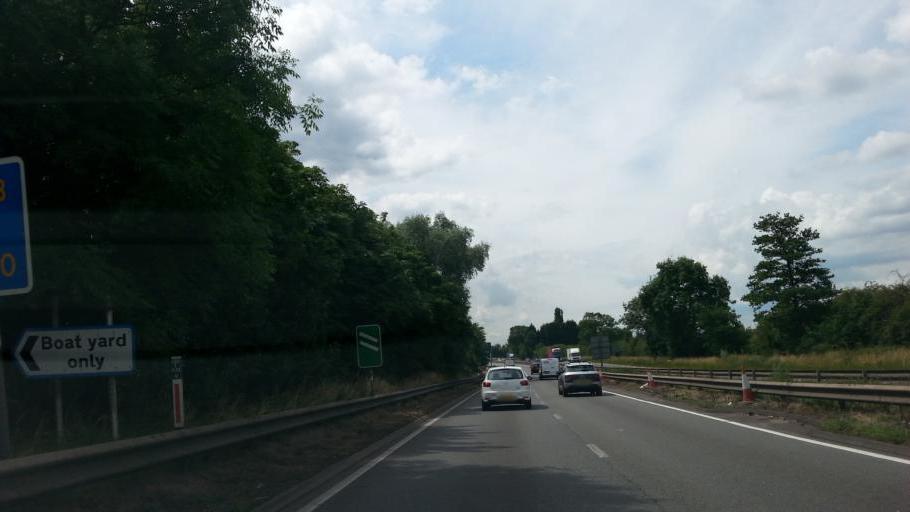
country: GB
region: England
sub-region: Staffordshire
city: Whittington
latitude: 52.6976
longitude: -1.7829
